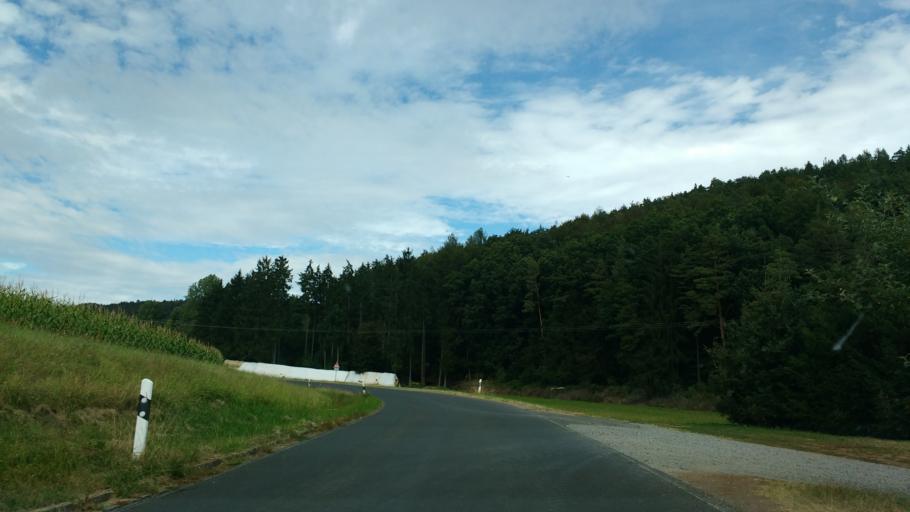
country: DE
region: Bavaria
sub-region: Regierungsbezirk Unterfranken
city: Geiselwind
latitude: 49.7830
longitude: 10.5226
